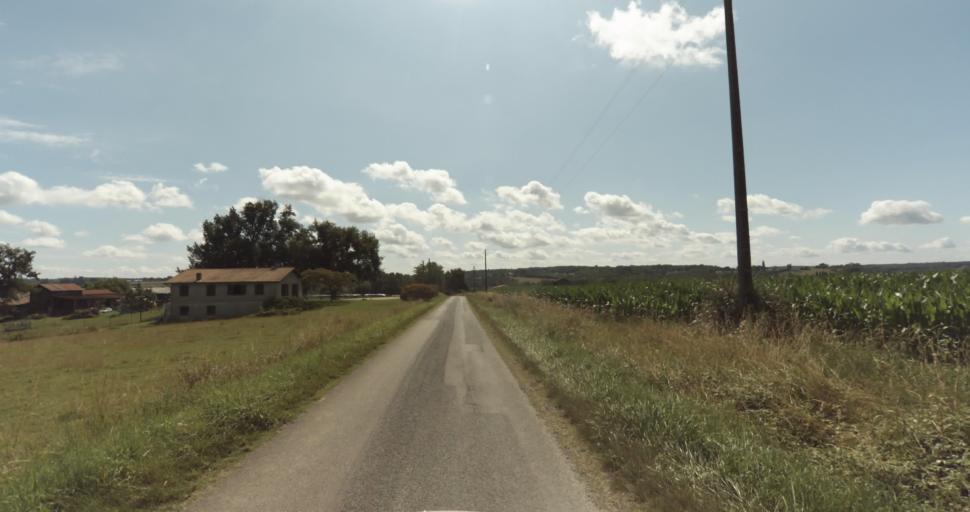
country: FR
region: Aquitaine
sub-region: Departement de la Gironde
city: Bazas
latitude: 44.4495
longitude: -0.1768
